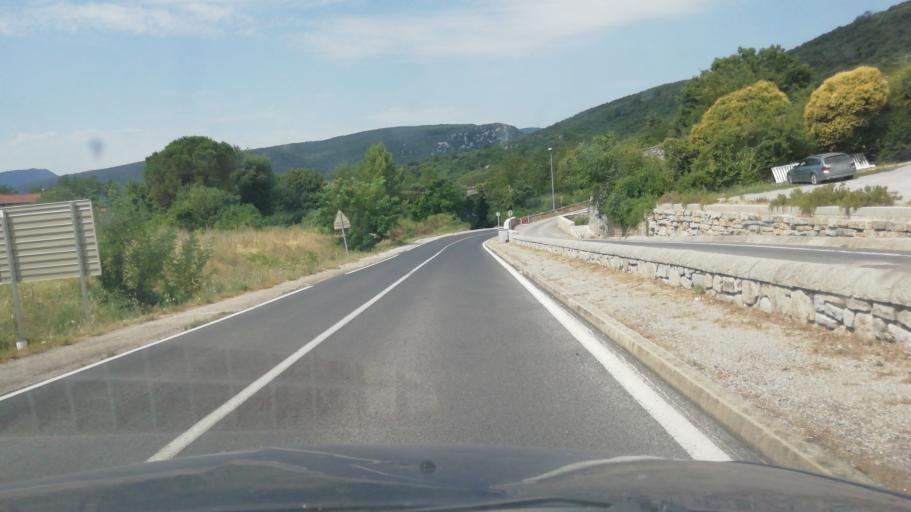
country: FR
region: Languedoc-Roussillon
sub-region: Departement de l'Herault
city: Ganges
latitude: 43.9443
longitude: 3.7153
